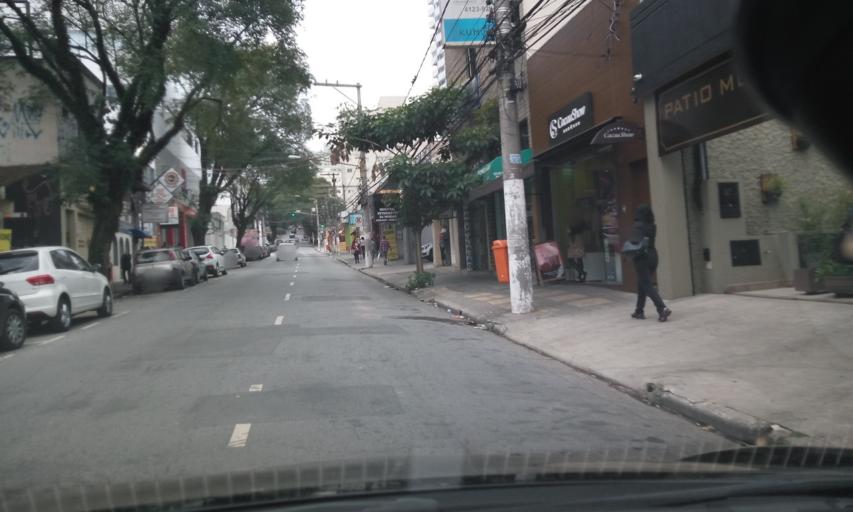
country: BR
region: Sao Paulo
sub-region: Sao Bernardo Do Campo
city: Sao Bernardo do Campo
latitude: -23.7115
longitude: -46.5495
